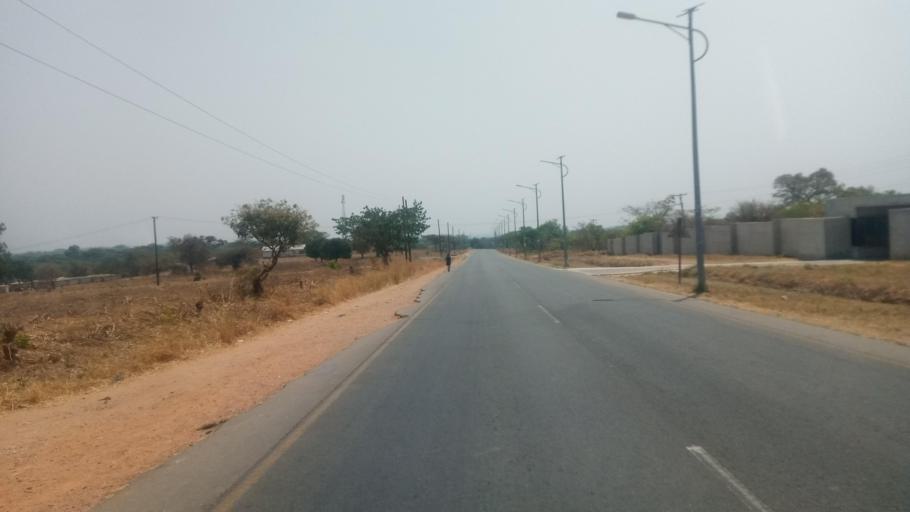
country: ZM
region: Lusaka
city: Lusaka
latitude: -15.4652
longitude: 28.4322
